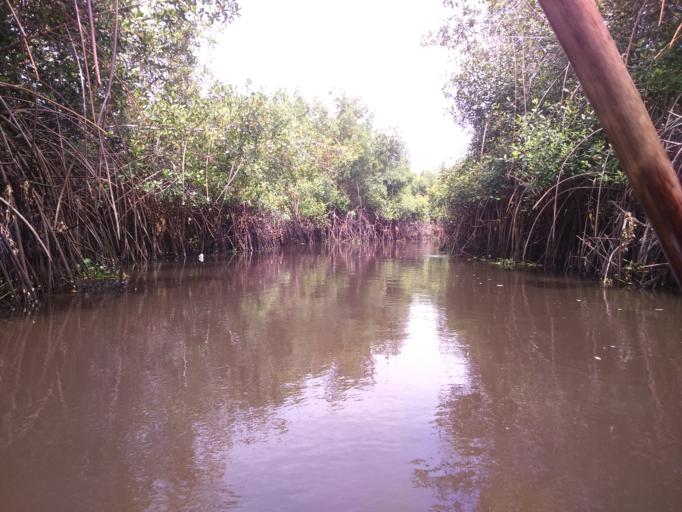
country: BJ
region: Mono
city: Grand-Popo
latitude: 6.3096
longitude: 1.9165
